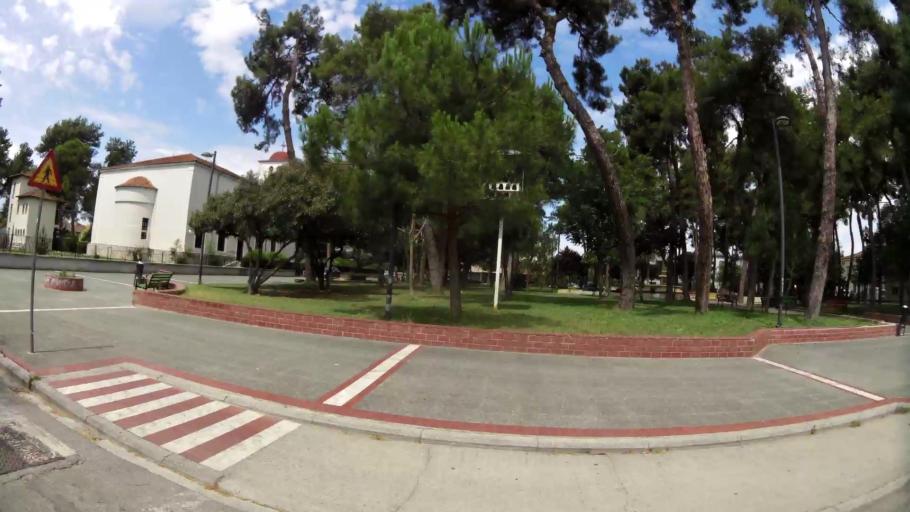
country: GR
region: Central Macedonia
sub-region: Nomos Pierias
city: Katerini
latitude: 40.2770
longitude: 22.5024
